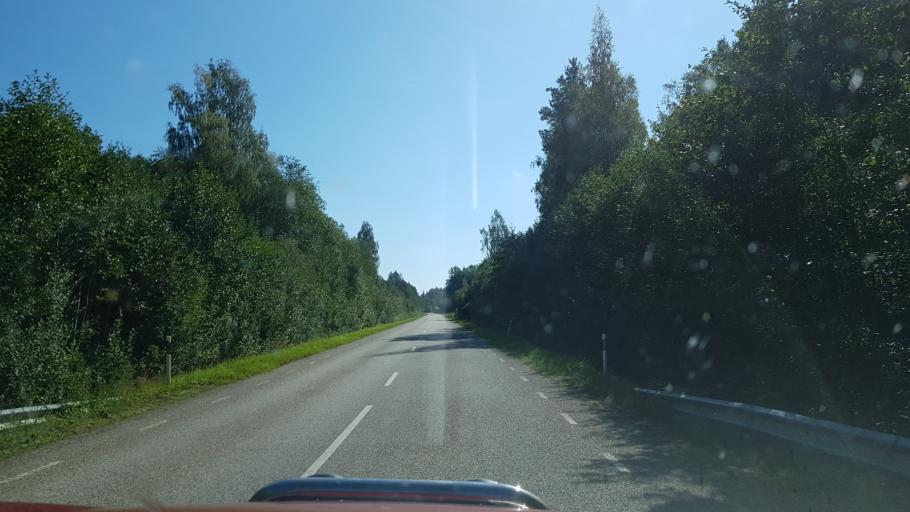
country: EE
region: Polvamaa
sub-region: Polva linn
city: Polva
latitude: 58.2499
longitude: 27.1845
